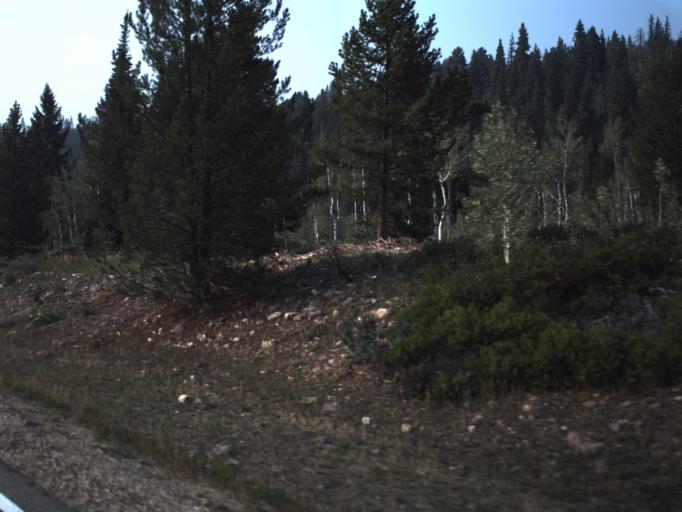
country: US
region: Utah
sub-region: Summit County
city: Francis
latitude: 40.5918
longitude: -111.0699
